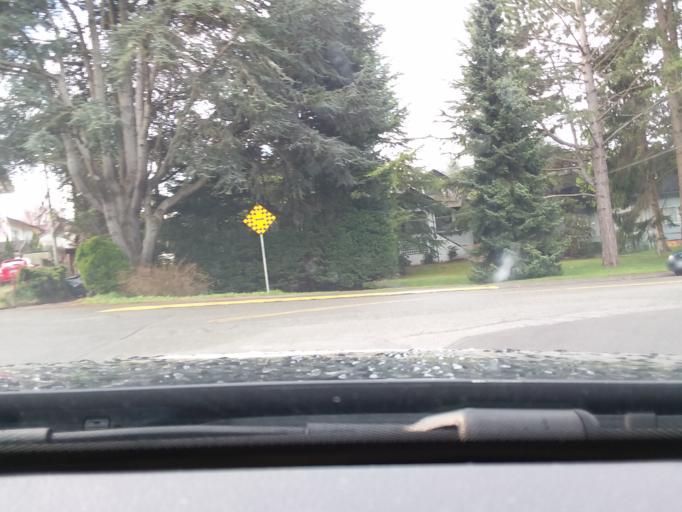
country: CA
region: British Columbia
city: Victoria
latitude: 48.4389
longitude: -123.4033
